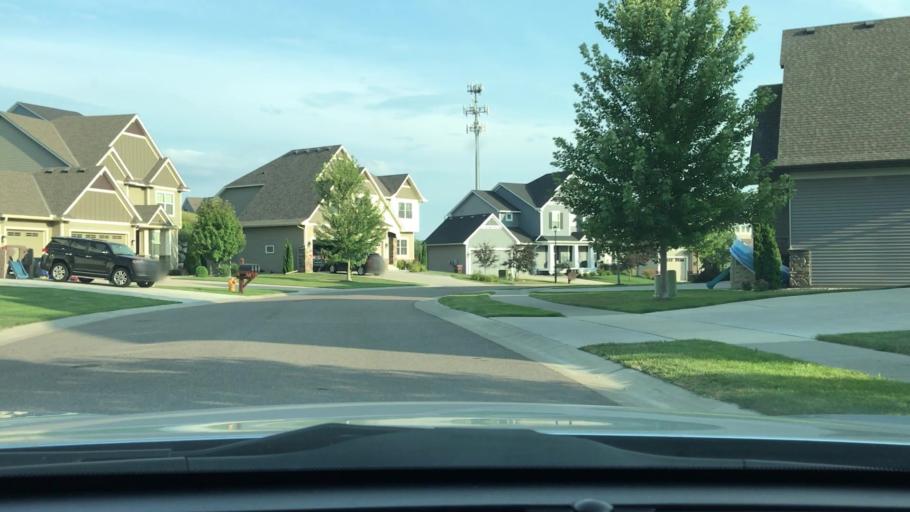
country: US
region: Minnesota
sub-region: Hennepin County
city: Maple Grove
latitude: 45.0531
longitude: -93.4731
